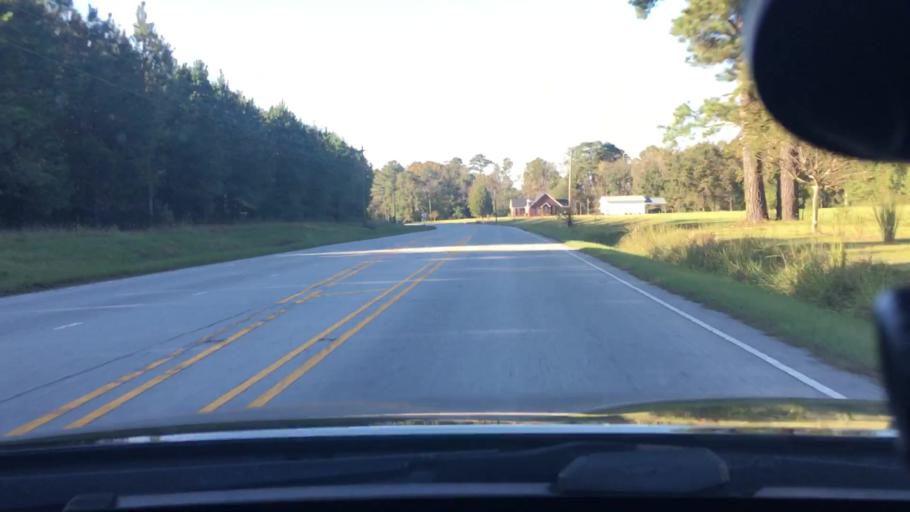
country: US
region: North Carolina
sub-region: Craven County
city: Vanceboro
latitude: 35.3333
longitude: -77.1721
